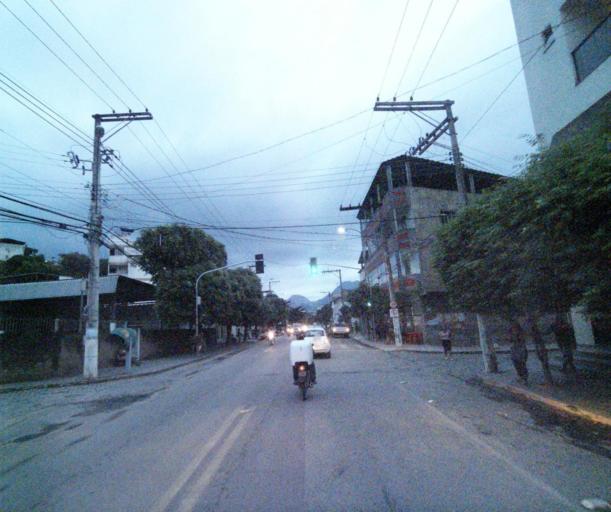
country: BR
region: Espirito Santo
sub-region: Castelo
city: Castelo
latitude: -20.6179
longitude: -41.2043
